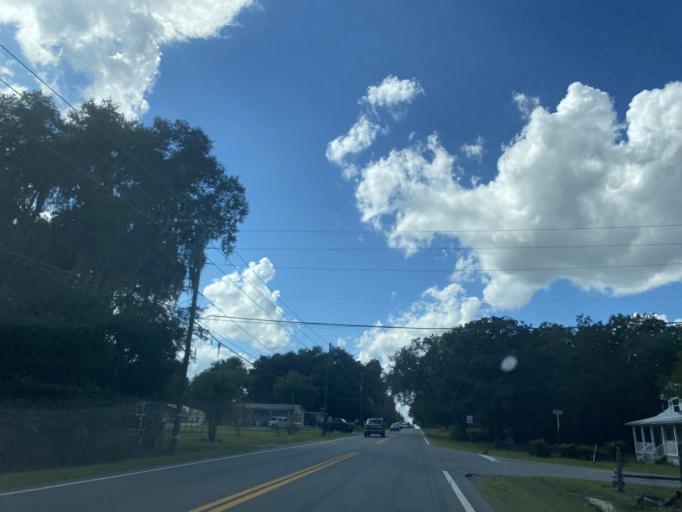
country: US
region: Florida
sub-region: Sumter County
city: The Villages
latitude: 28.9820
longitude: -81.9787
